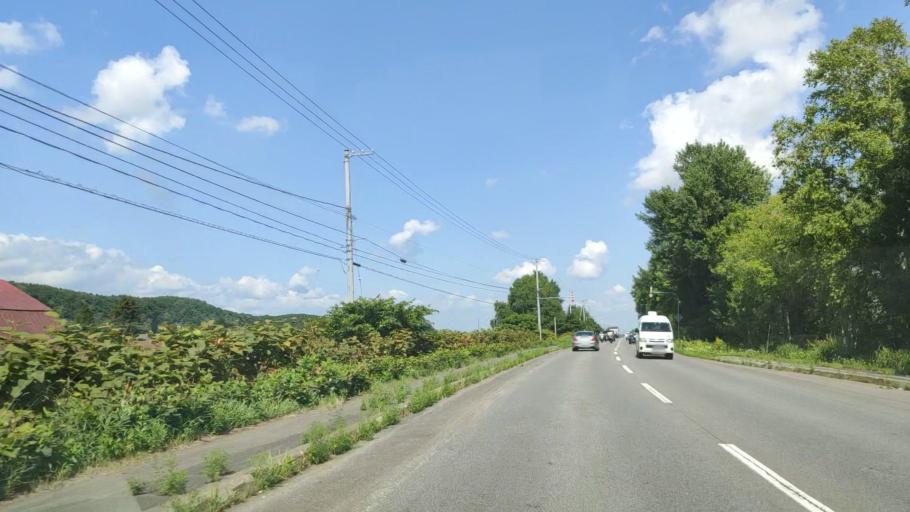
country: JP
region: Hokkaido
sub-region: Asahikawa-shi
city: Asahikawa
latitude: 43.6329
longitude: 142.4581
